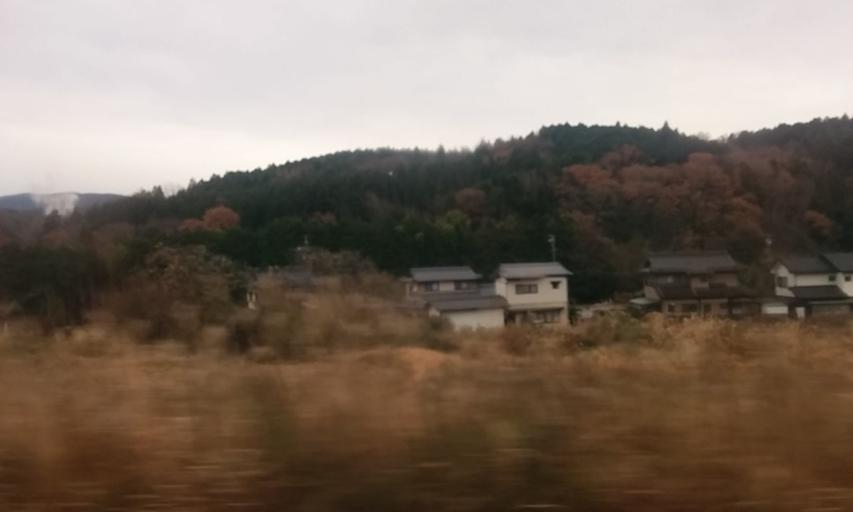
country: JP
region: Gifu
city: Mizunami
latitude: 35.4351
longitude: 137.3507
